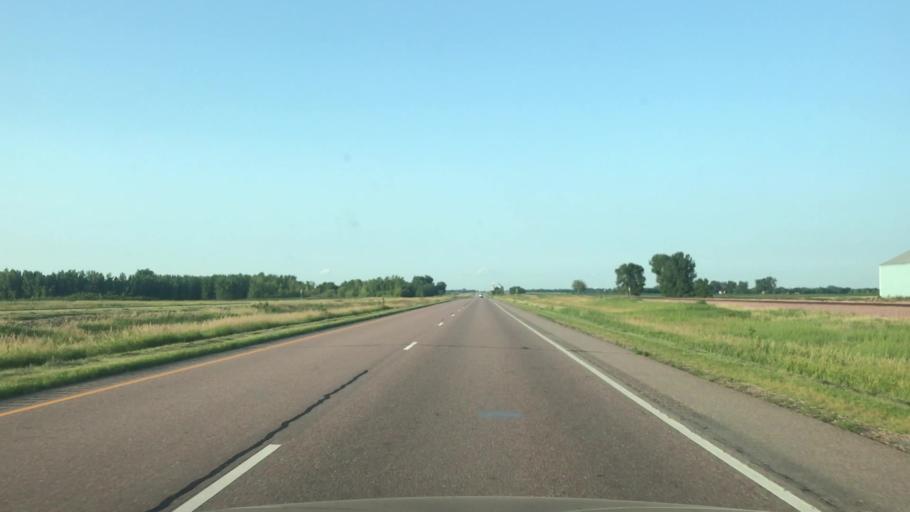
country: US
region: Minnesota
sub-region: Jackson County
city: Lakefield
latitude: 43.7687
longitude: -95.3635
